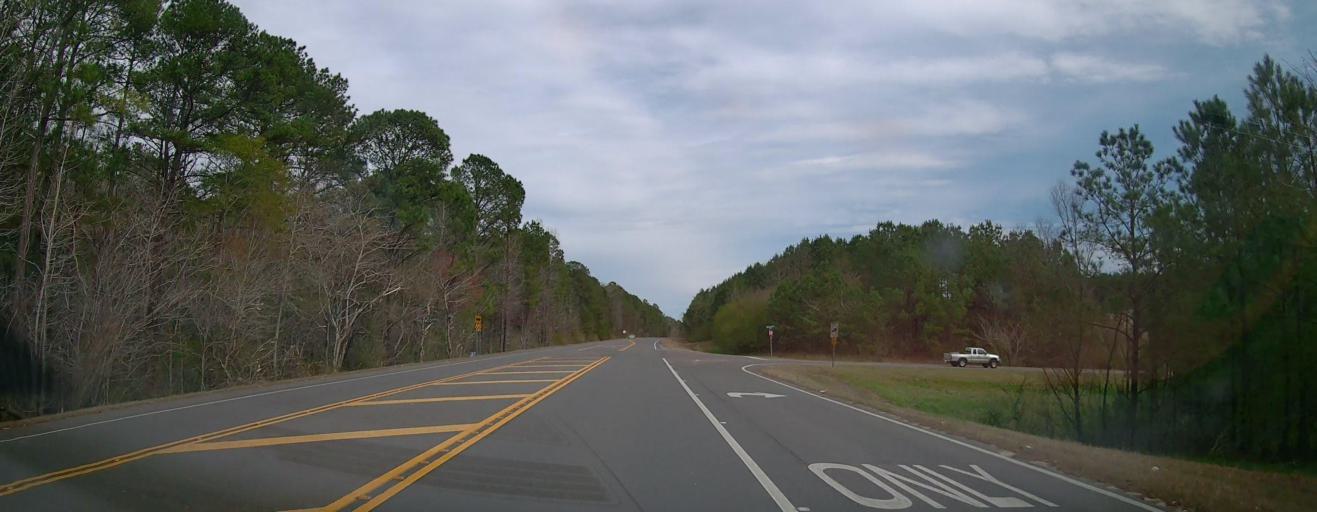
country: US
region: Alabama
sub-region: Walker County
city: Jasper
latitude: 33.8634
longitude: -87.3937
